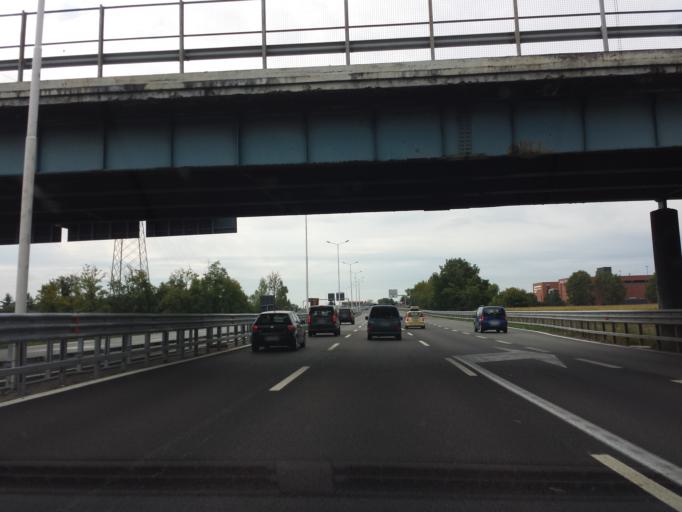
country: IT
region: Lombardy
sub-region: Citta metropolitana di Milano
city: Figino
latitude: 45.4933
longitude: 9.0665
